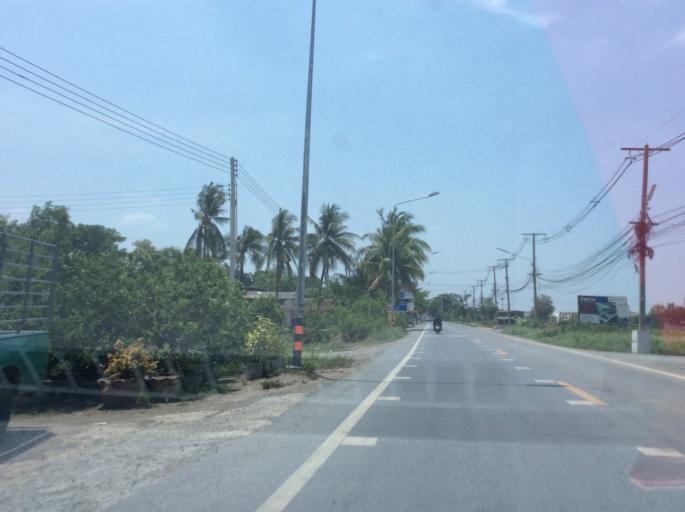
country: TH
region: Pathum Thani
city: Ban Rangsit
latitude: 14.0166
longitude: 100.7796
